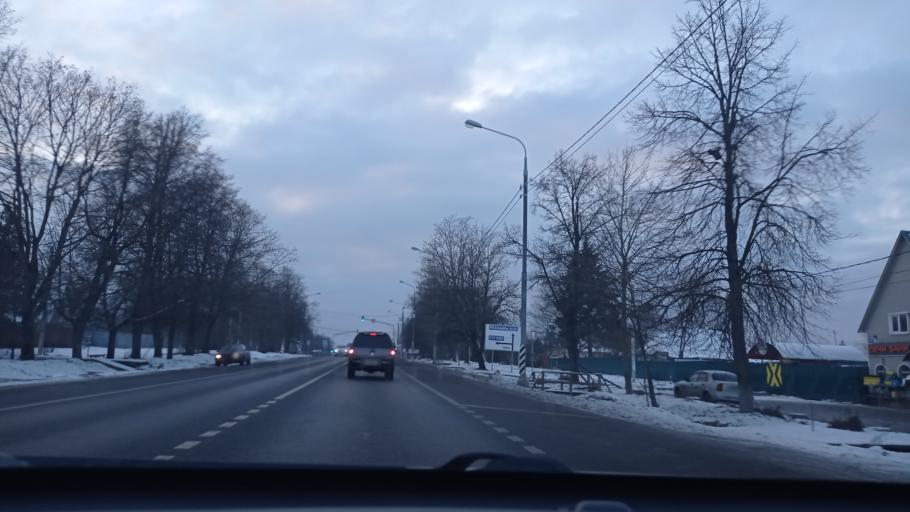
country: RU
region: Moskovskaya
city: Kievskij
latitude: 55.2376
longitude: 37.0394
